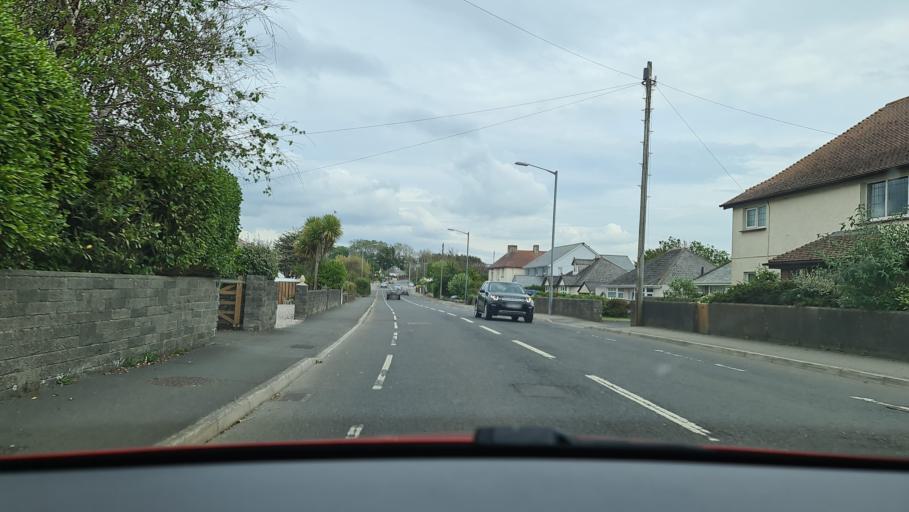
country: GB
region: England
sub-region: Cornwall
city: Bude
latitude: 50.8214
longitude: -4.5388
